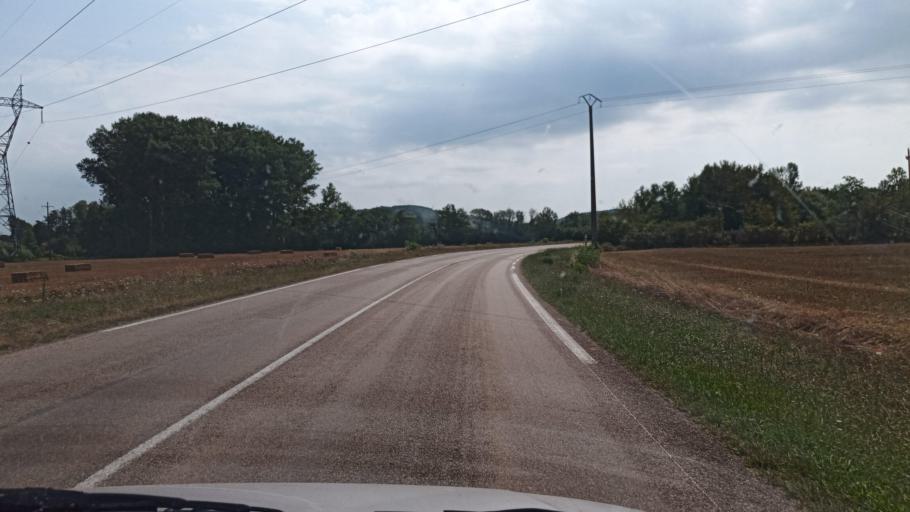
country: FR
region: Bourgogne
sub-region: Departement de l'Yonne
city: Villeneuve-sur-Yonne
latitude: 48.0953
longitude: 3.2841
